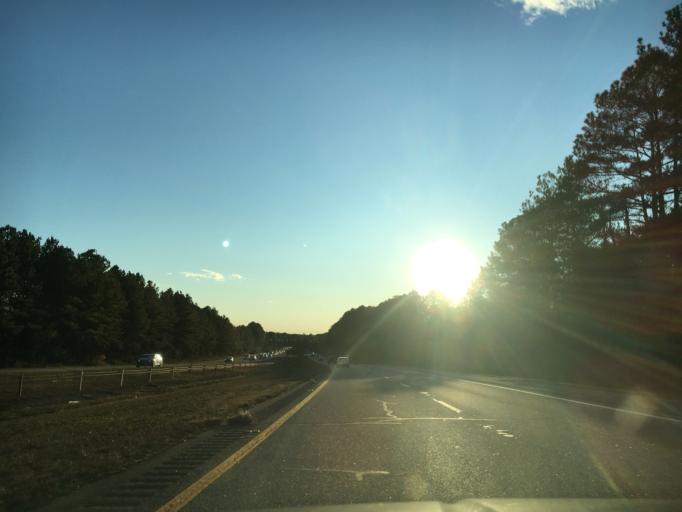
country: US
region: South Carolina
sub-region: Richland County
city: Forest Acres
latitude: 34.0460
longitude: -81.0110
